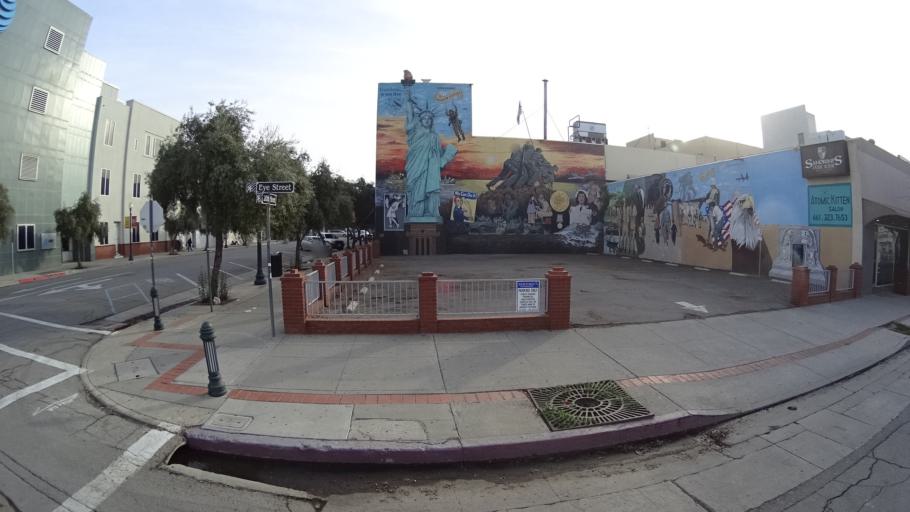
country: US
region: California
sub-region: Kern County
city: Bakersfield
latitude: 35.3770
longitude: -119.0200
